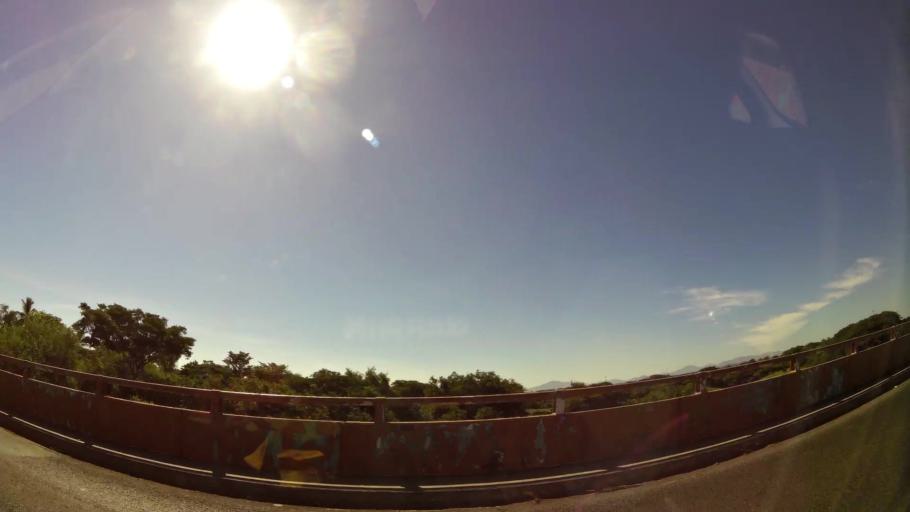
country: SV
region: San Miguel
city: San Miguel
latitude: 13.4604
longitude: -88.1520
